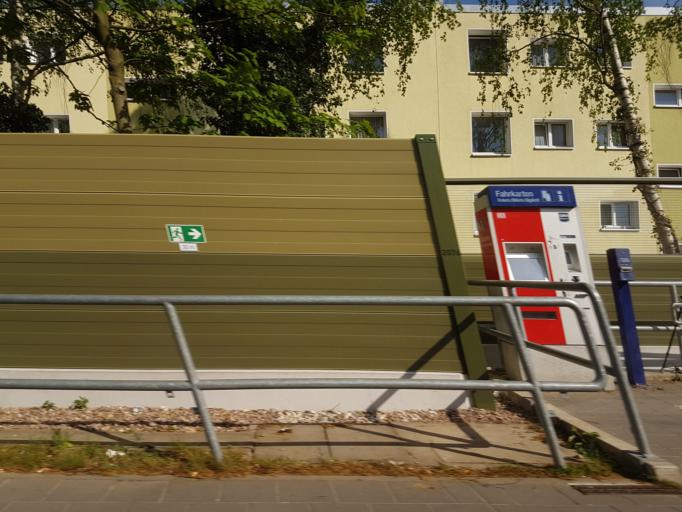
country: DE
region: Lower Saxony
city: Ronnenberg
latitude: 52.3395
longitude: 9.6684
